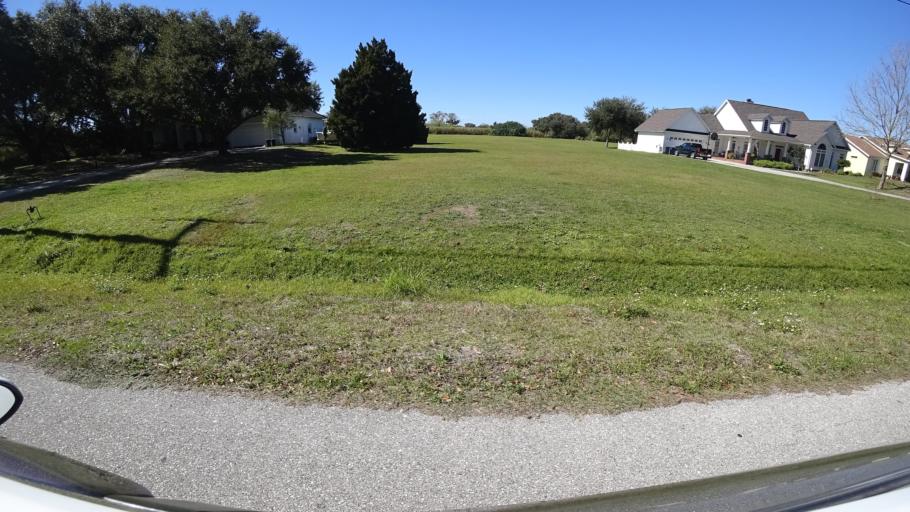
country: US
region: Florida
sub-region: Manatee County
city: Memphis
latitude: 27.5706
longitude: -82.5482
